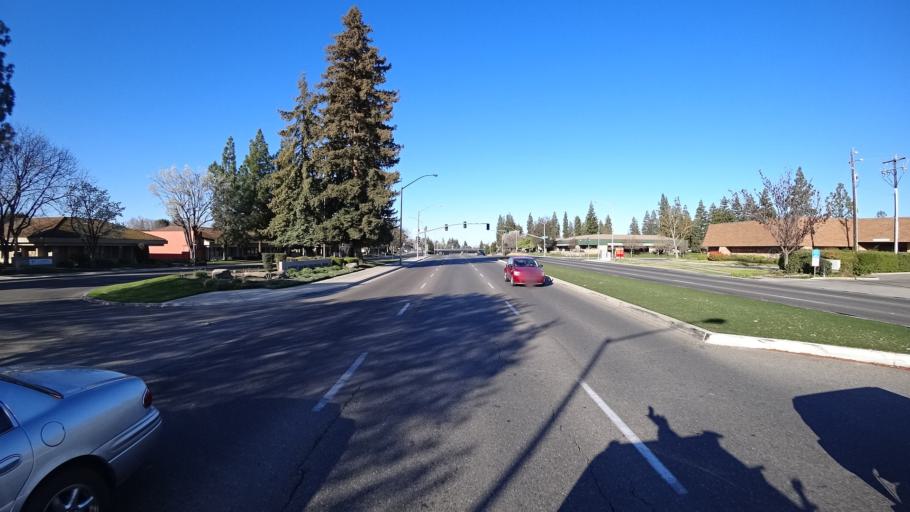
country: US
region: California
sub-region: Fresno County
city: Fresno
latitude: 36.8082
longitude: -119.8375
